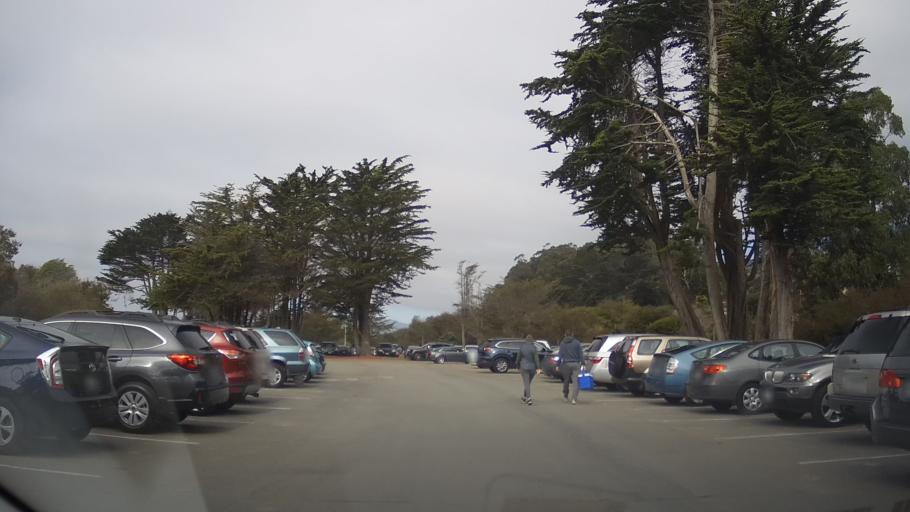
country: US
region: California
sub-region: Marin County
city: Bolinas
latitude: 37.8967
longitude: -122.6392
